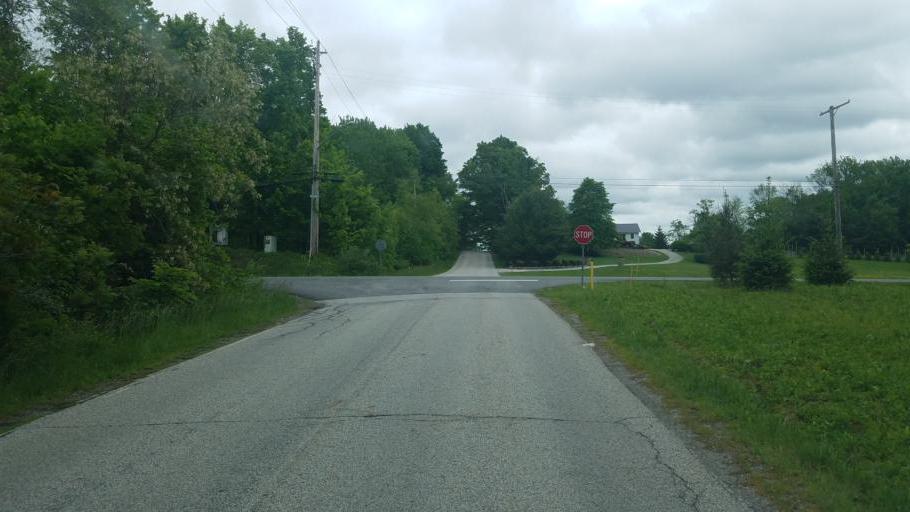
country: US
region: Ohio
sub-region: Geauga County
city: Bainbridge
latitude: 41.3774
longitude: -81.2467
